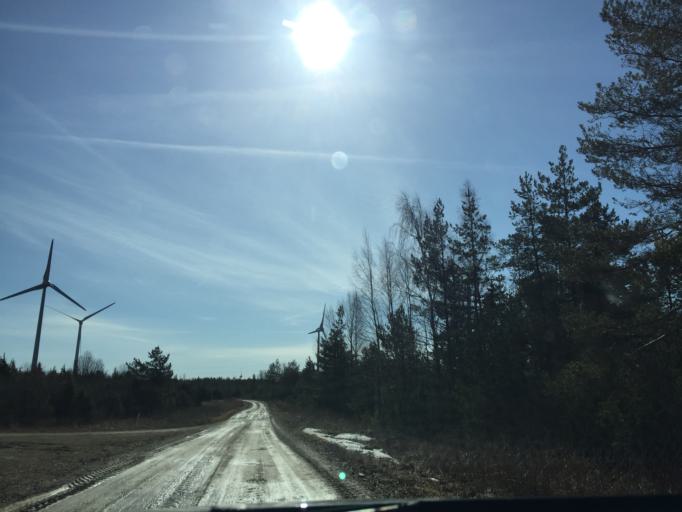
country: EE
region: Laeaene
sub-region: Haapsalu linn
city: Haapsalu
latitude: 58.6366
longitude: 23.5212
